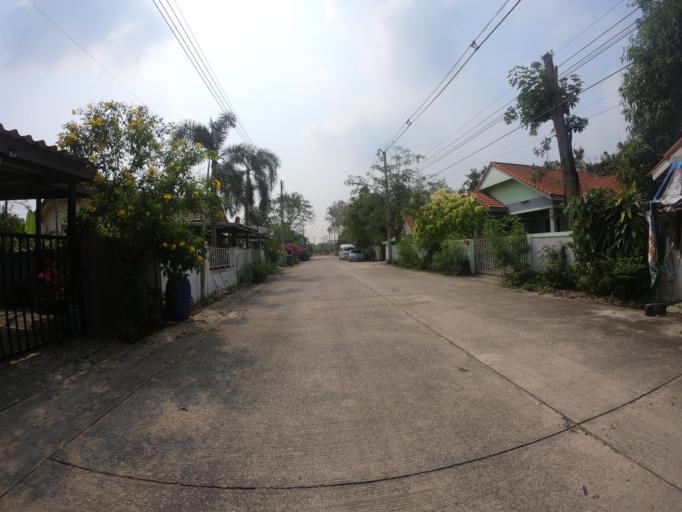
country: TH
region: Pathum Thani
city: Nong Suea
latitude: 14.0680
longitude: 100.8534
